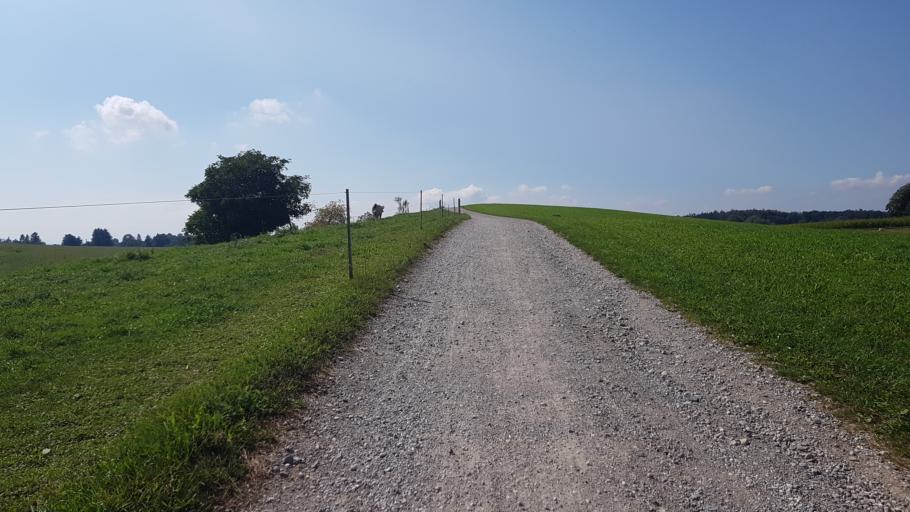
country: DE
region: Bavaria
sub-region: Upper Bavaria
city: Worthsee
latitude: 48.0483
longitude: 11.1963
